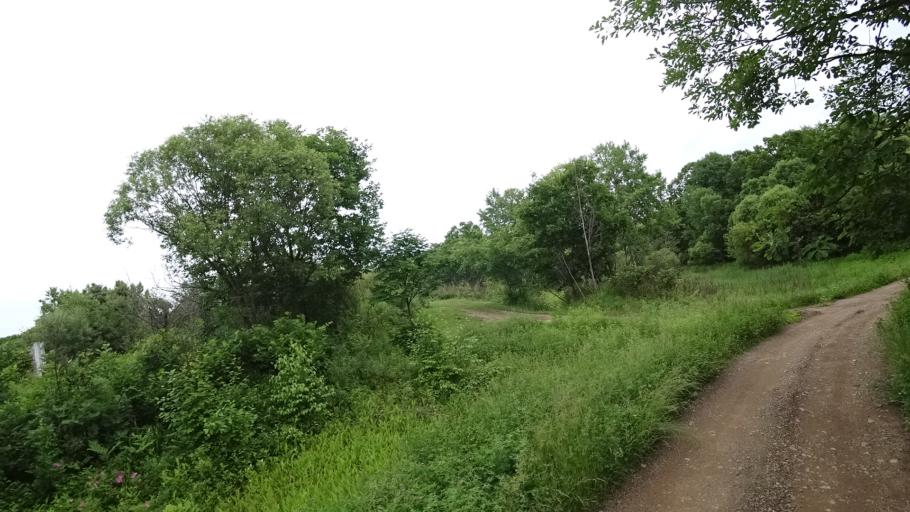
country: RU
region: Primorskiy
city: Novosysoyevka
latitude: 44.2099
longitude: 133.3279
